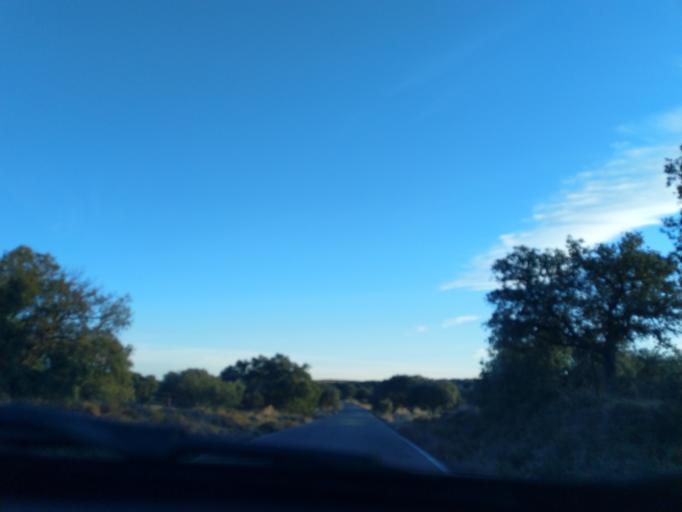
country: ES
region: Extremadura
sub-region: Provincia de Badajoz
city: Valverde de Llerena
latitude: 38.2408
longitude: -5.8244
